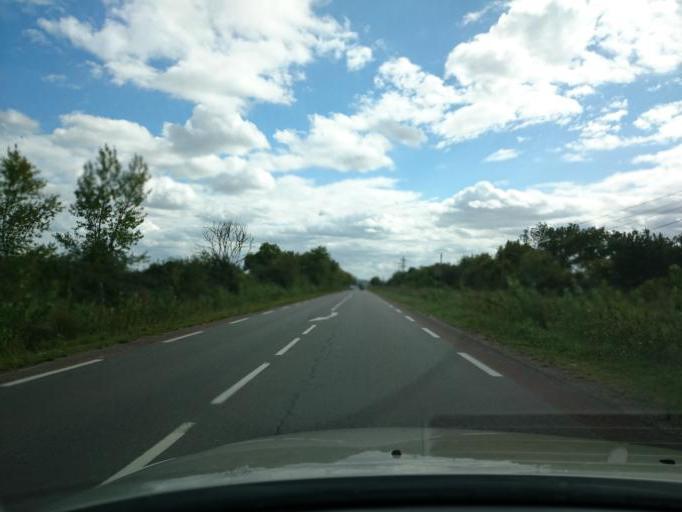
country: FR
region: Aquitaine
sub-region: Departement de la Gironde
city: Bassens
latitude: 44.9105
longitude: -0.5579
